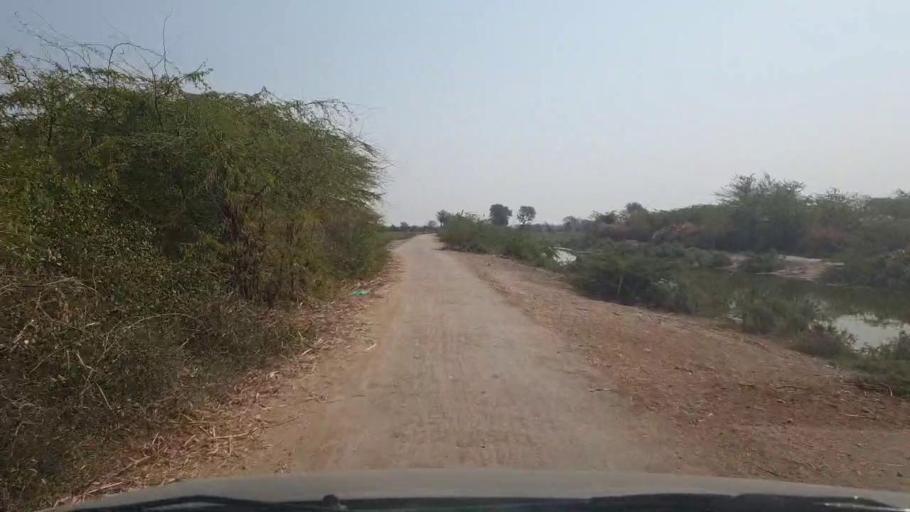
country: PK
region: Sindh
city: Mirwah Gorchani
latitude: 25.2928
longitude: 69.1448
